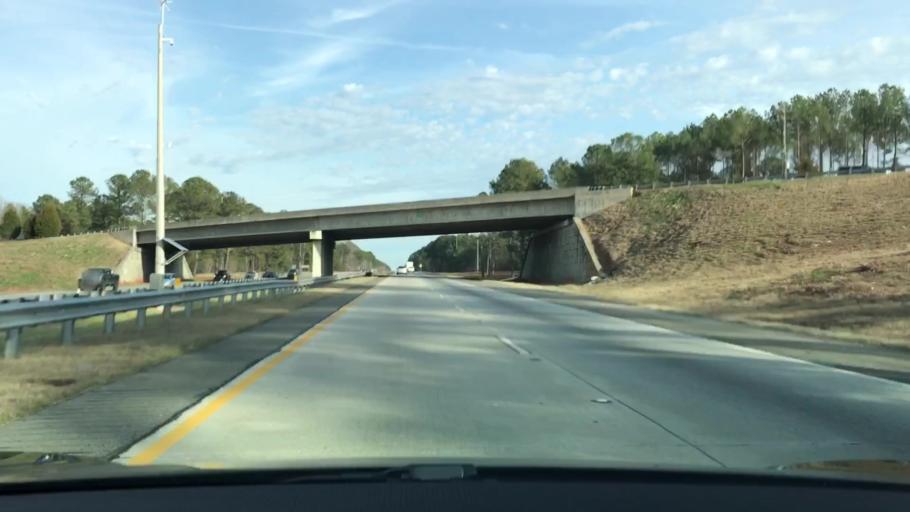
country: US
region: Georgia
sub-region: Greene County
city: Greensboro
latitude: 33.5457
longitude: -83.2067
